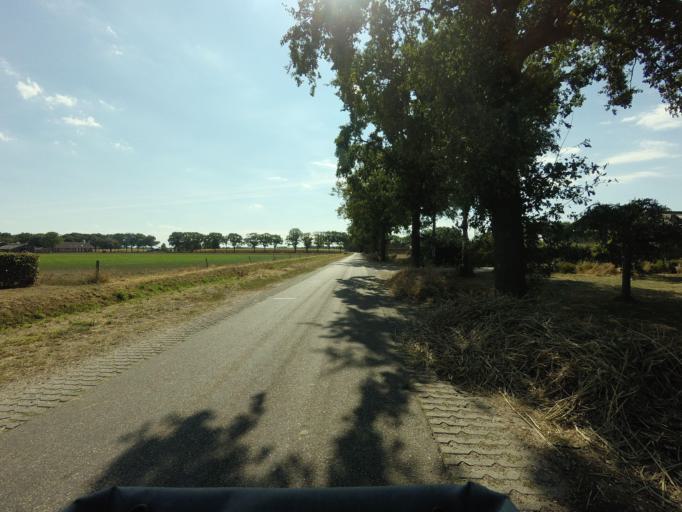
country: NL
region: North Brabant
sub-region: Gemeente Someren
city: Someren
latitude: 51.3559
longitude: 5.6681
